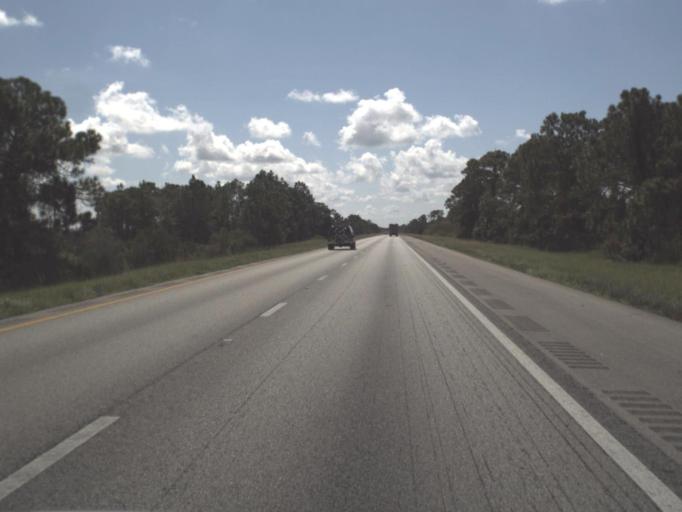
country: US
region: Florida
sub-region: Lee County
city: Burnt Store Marina
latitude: 26.8215
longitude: -81.9446
